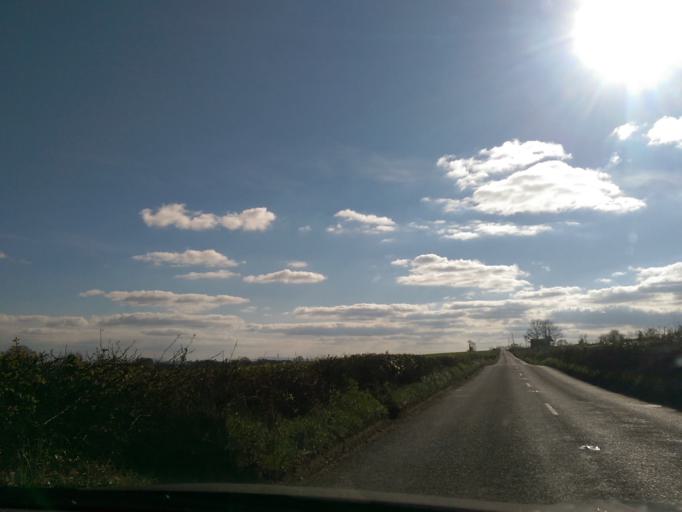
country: IE
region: Connaught
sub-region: County Galway
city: Portumna
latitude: 53.1054
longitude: -8.1340
